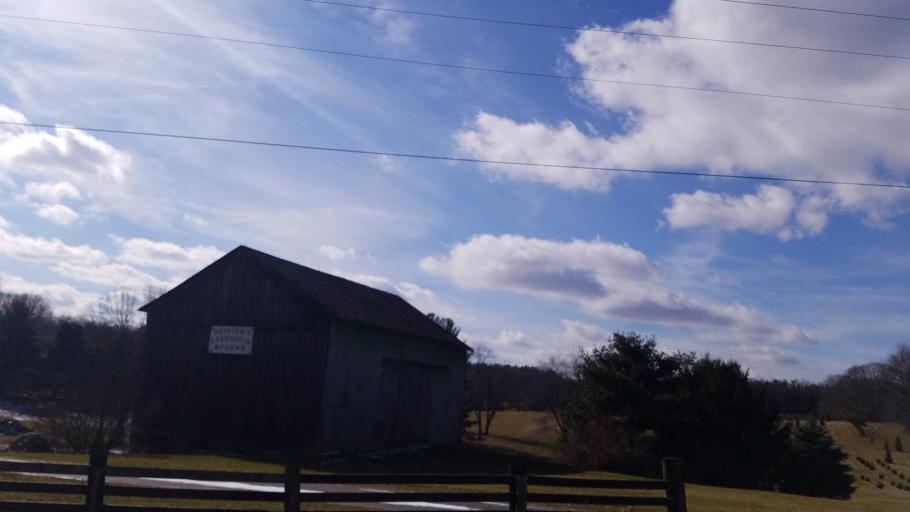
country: US
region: Ohio
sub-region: Richland County
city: Lexington
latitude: 40.7142
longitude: -82.6121
